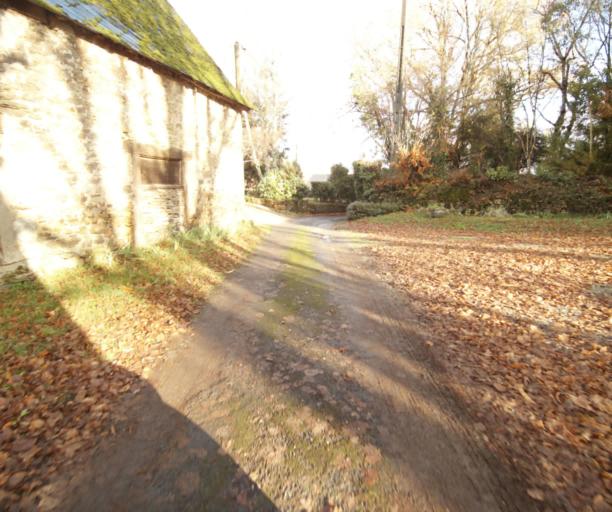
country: FR
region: Limousin
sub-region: Departement de la Correze
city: Saint-Mexant
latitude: 45.2566
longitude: 1.6229
